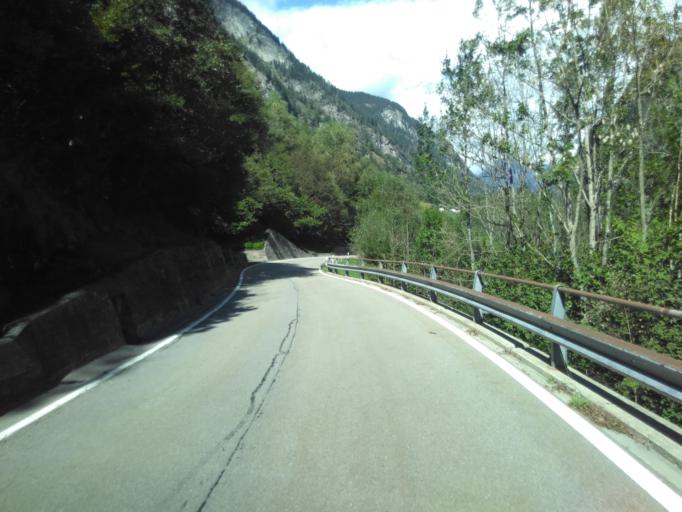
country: CH
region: Grisons
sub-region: Moesa District
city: Cauco
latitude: 46.3265
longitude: 9.1183
